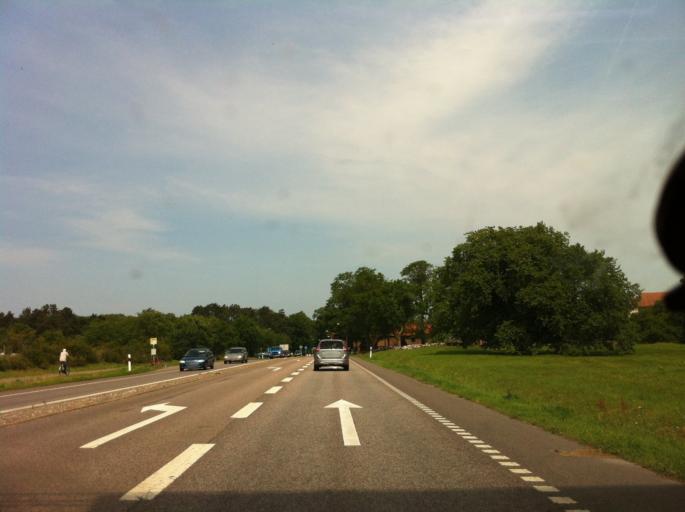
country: SE
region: Kalmar
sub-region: Borgholms Kommun
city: Borgholm
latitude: 56.8658
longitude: 16.6556
